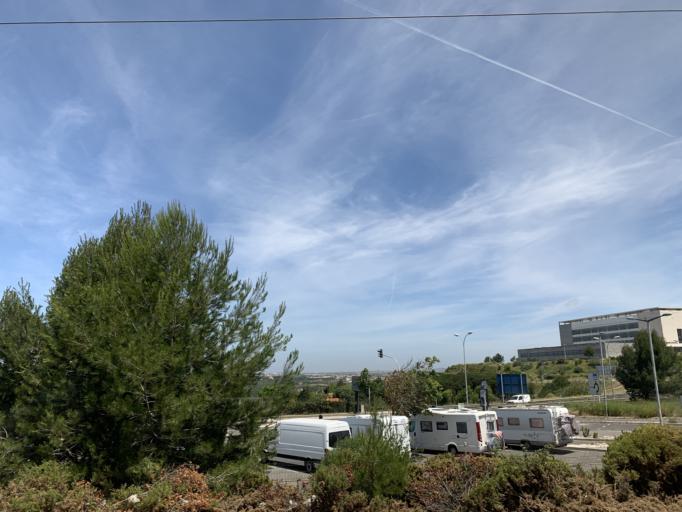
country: PT
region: Lisbon
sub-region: Sintra
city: Sintra
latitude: 38.8024
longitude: -9.3736
